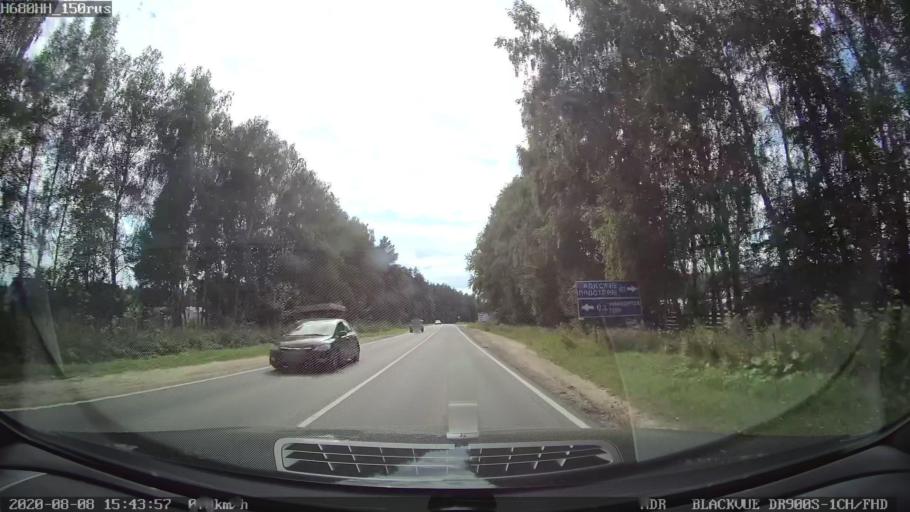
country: RU
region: Tula
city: Zaokskiy
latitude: 54.7318
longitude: 37.3345
